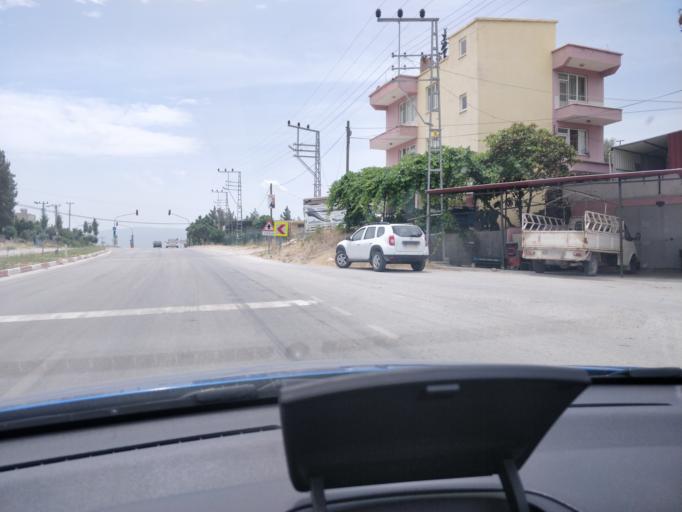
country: TR
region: Mersin
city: Mut
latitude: 36.6178
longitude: 33.4414
